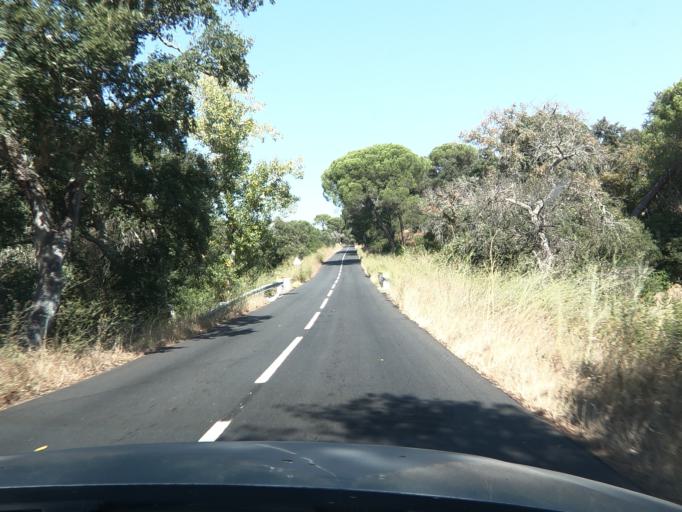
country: PT
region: Setubal
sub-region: Alcacer do Sal
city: Alcacer do Sal
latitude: 38.3191
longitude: -8.4394
